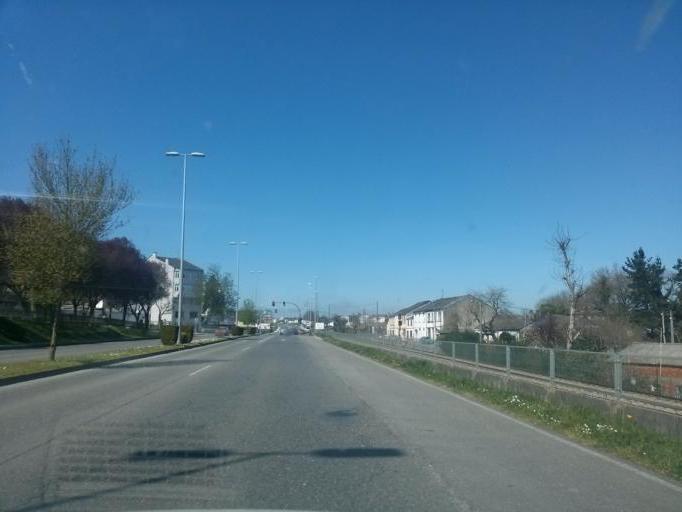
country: ES
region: Galicia
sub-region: Provincia de Lugo
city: Lugo
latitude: 43.0278
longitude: -7.5610
